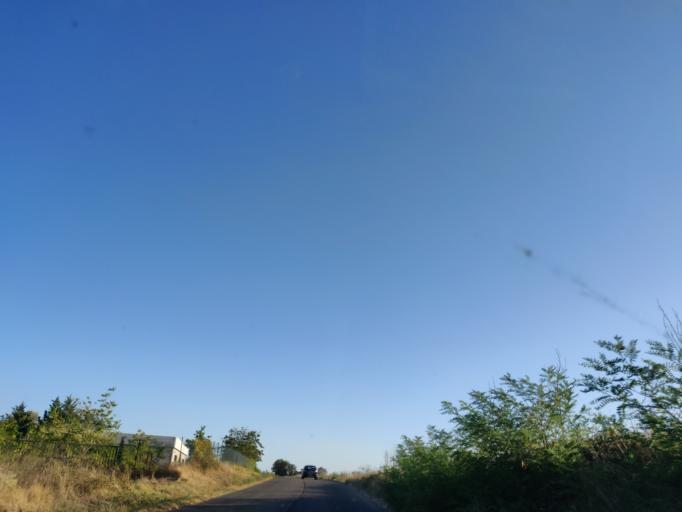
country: IT
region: Latium
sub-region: Provincia di Viterbo
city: Grotte di Castro
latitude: 42.6947
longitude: 11.8780
